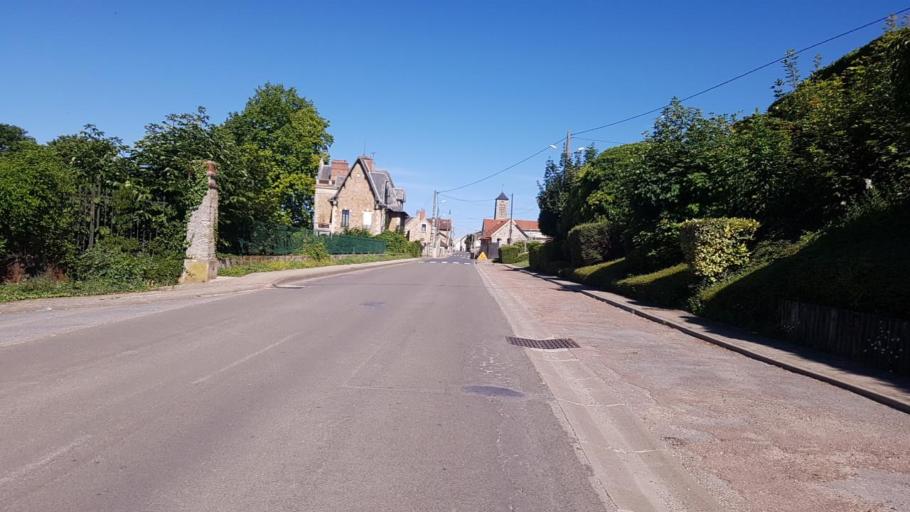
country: FR
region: Picardie
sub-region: Departement de l'Aisne
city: Charly-sur-Marne
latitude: 48.9733
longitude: 3.3110
